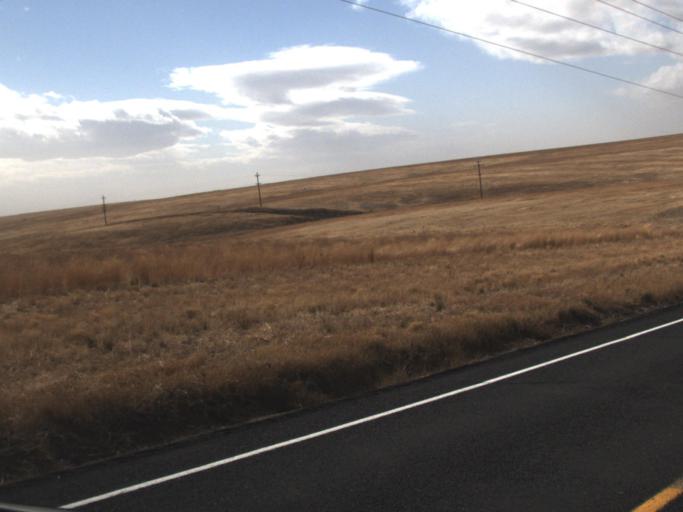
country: US
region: Washington
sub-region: Okanogan County
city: Coulee Dam
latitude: 47.6125
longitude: -118.7399
